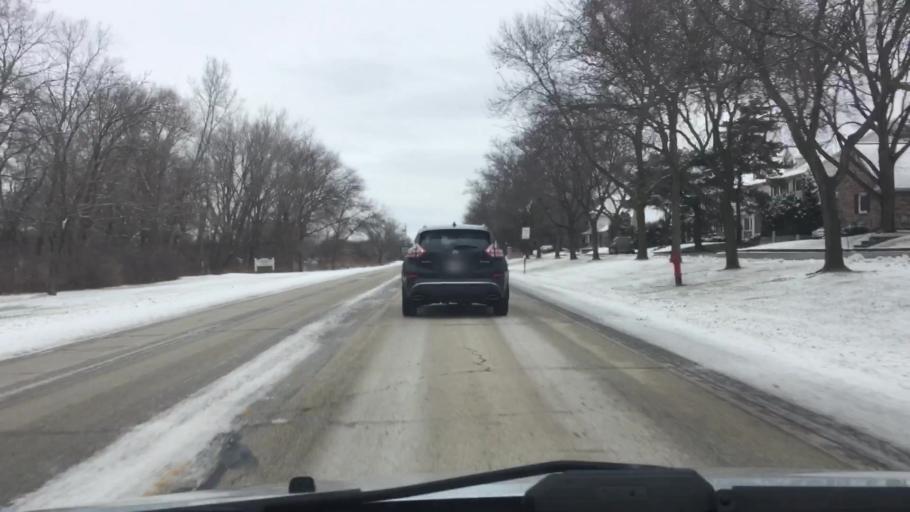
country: US
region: Wisconsin
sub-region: Waukesha County
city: Brookfield
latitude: 43.0433
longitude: -88.1061
